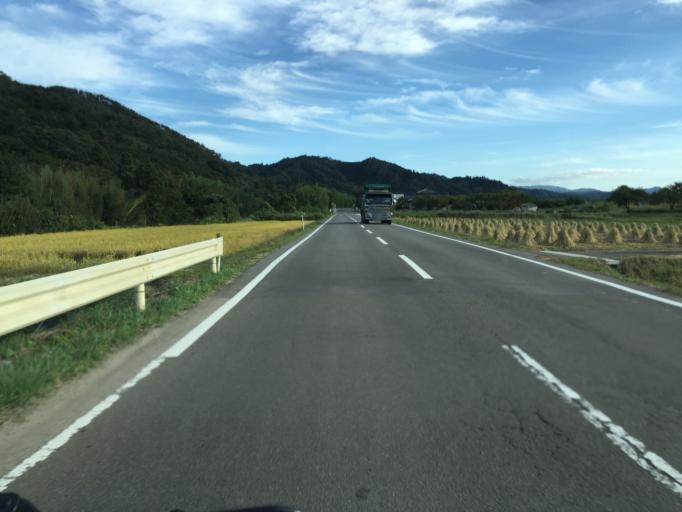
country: JP
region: Fukushima
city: Yanagawamachi-saiwaicho
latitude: 37.8248
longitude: 140.6161
